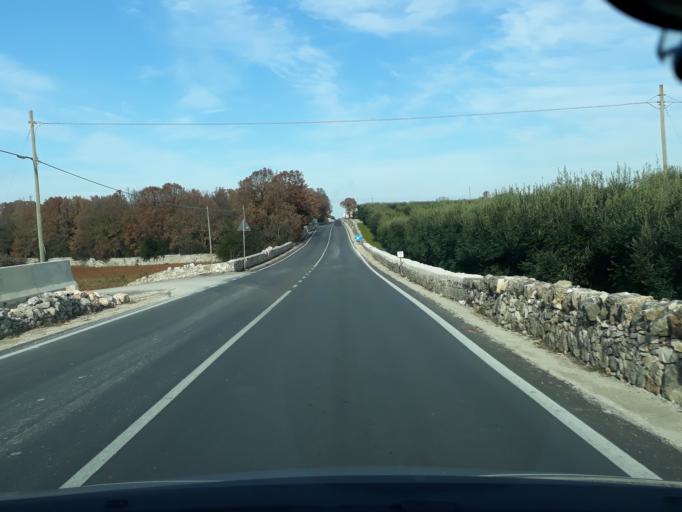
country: IT
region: Apulia
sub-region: Provincia di Bari
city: Locorotondo
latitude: 40.7696
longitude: 17.3337
